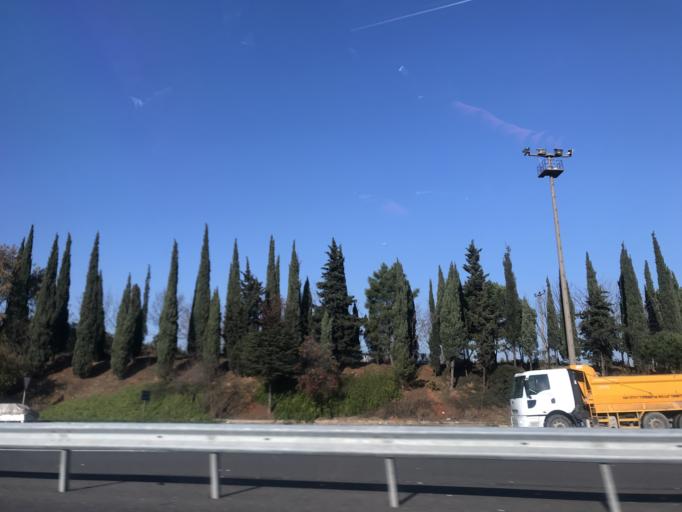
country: TR
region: Istanbul
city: Umraniye
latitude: 40.9932
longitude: 29.1694
